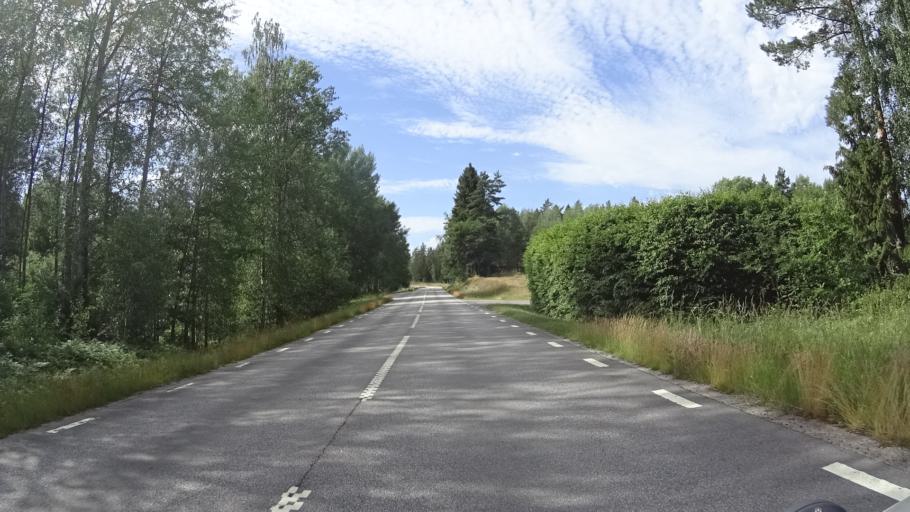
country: SE
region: OEstergoetland
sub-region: Atvidabergs Kommun
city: Atvidaberg
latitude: 58.1638
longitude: 16.0614
